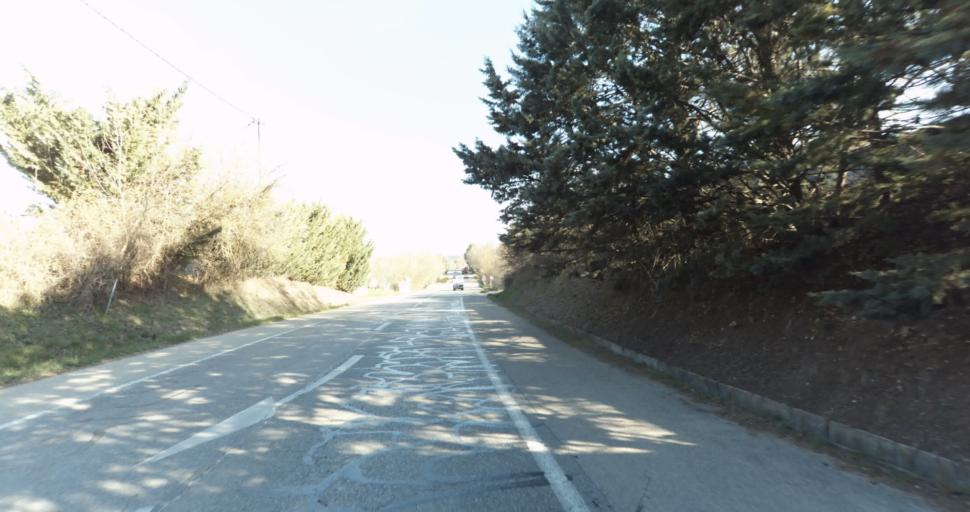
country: FR
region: Provence-Alpes-Cote d'Azur
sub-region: Departement des Bouches-du-Rhone
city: Aix-en-Provence
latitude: 43.5747
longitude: 5.4322
